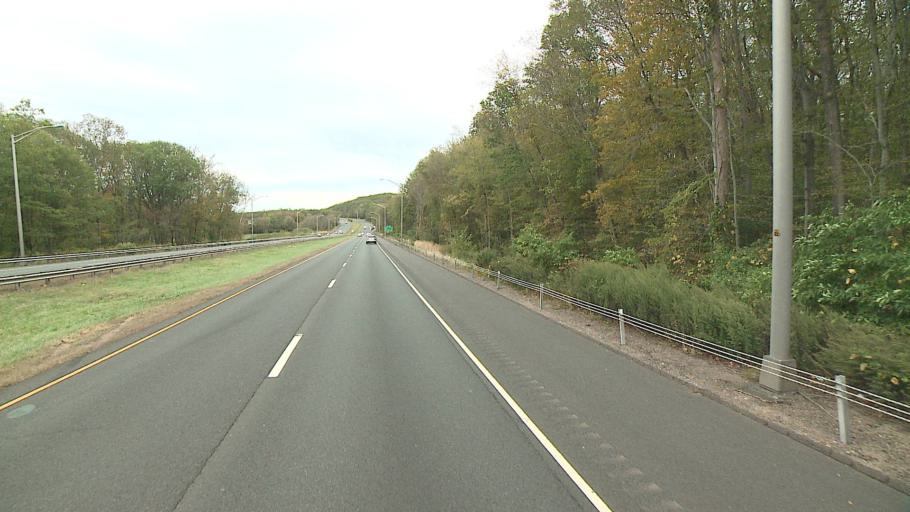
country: US
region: Connecticut
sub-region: Middlesex County
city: Higganum
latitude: 41.5188
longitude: -72.6040
